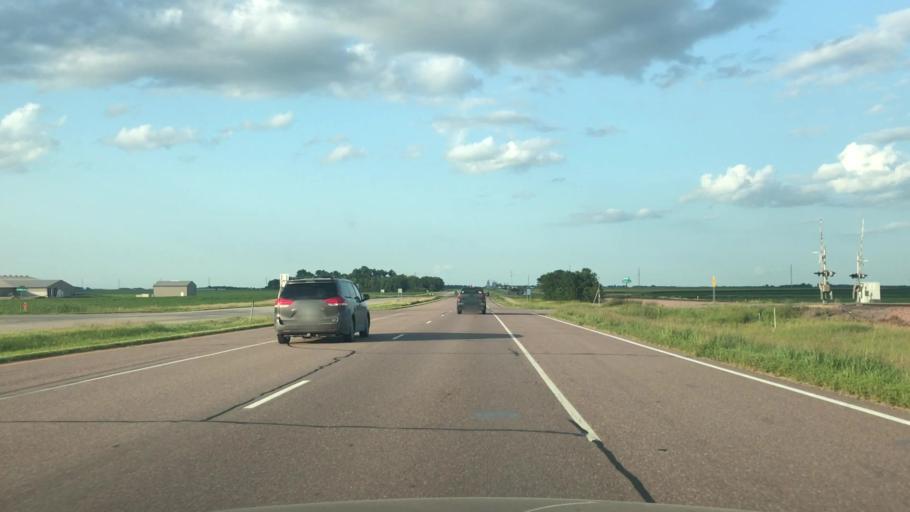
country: US
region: Minnesota
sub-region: Nobles County
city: Worthington
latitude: 43.6600
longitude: -95.5310
